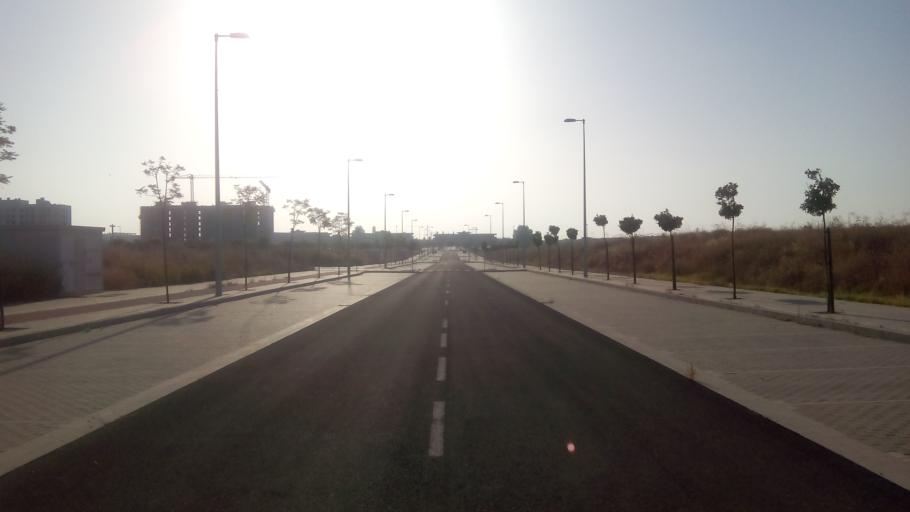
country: ES
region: Andalusia
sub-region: Province of Cordoba
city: Cordoba
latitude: 37.8898
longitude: -4.8151
